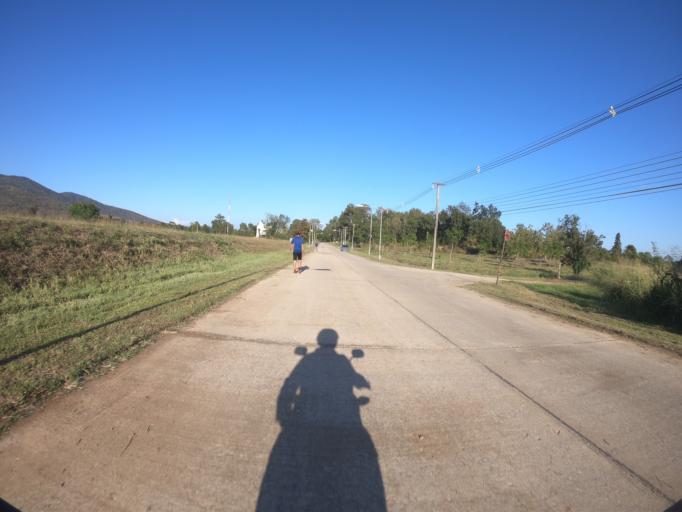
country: TH
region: Chiang Mai
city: Chiang Mai
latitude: 18.7593
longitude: 98.9304
